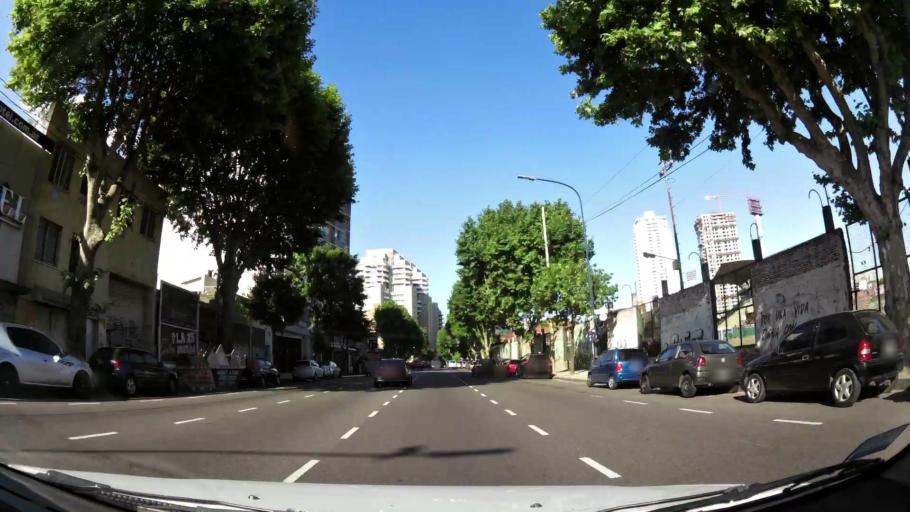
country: AR
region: Buenos Aires F.D.
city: Villa Santa Rita
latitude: -34.6187
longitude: -58.4499
